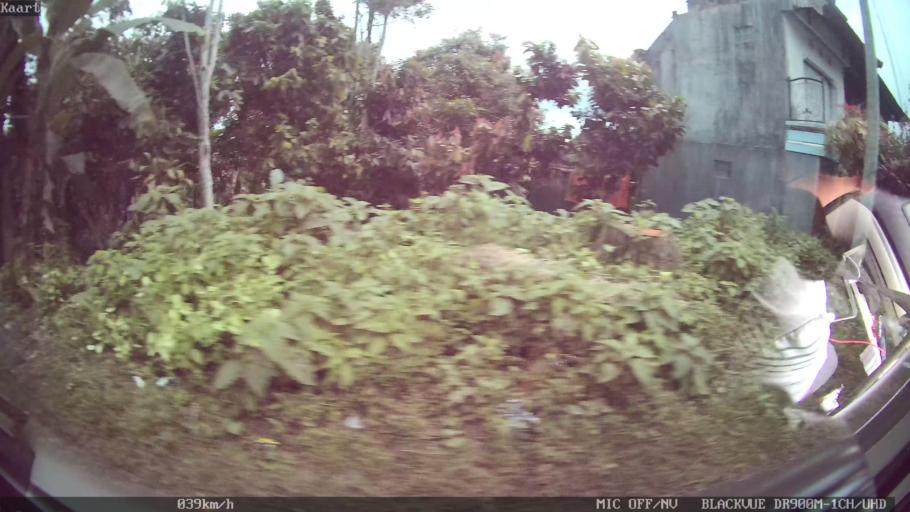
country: ID
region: Bali
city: Peneng
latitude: -8.3521
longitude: 115.2068
